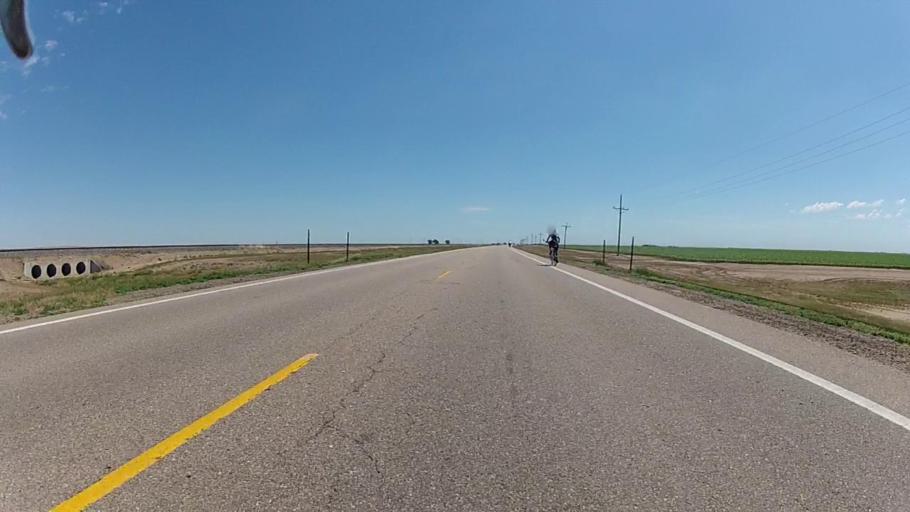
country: US
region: Kansas
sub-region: Gray County
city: Cimarron
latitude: 37.6590
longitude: -100.2199
